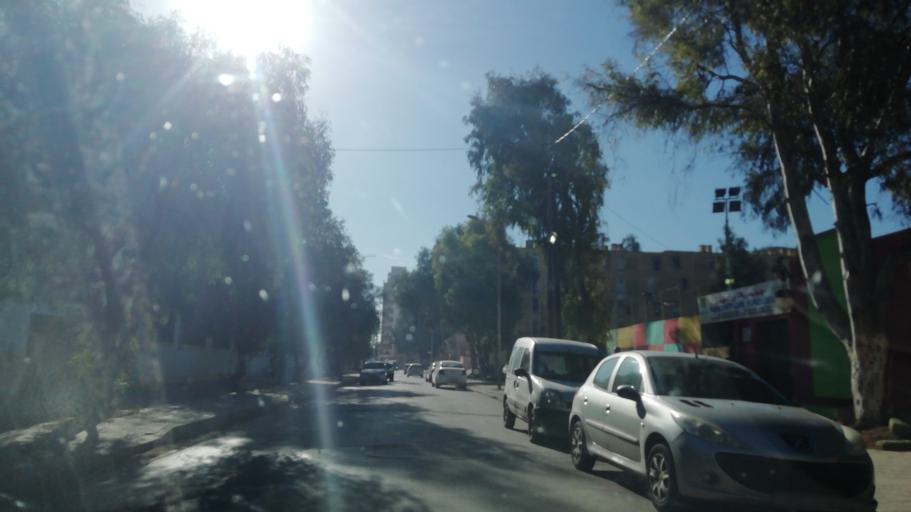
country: DZ
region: Oran
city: Oran
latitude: 35.6690
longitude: -0.6493
